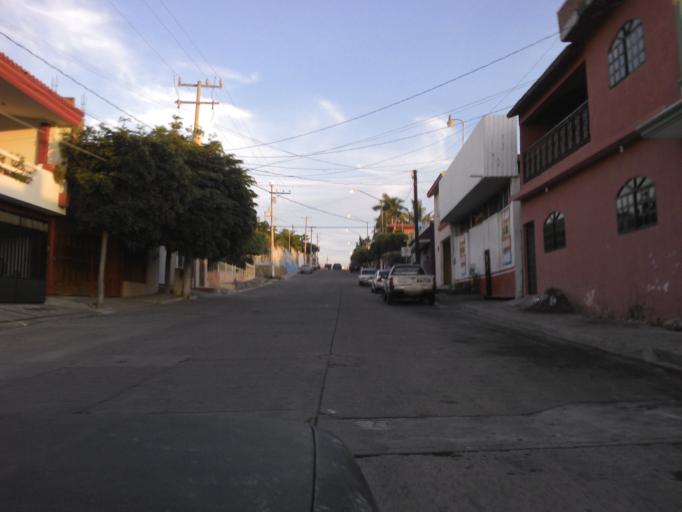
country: MX
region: Sinaloa
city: Culiacan
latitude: 24.7933
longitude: -107.4074
